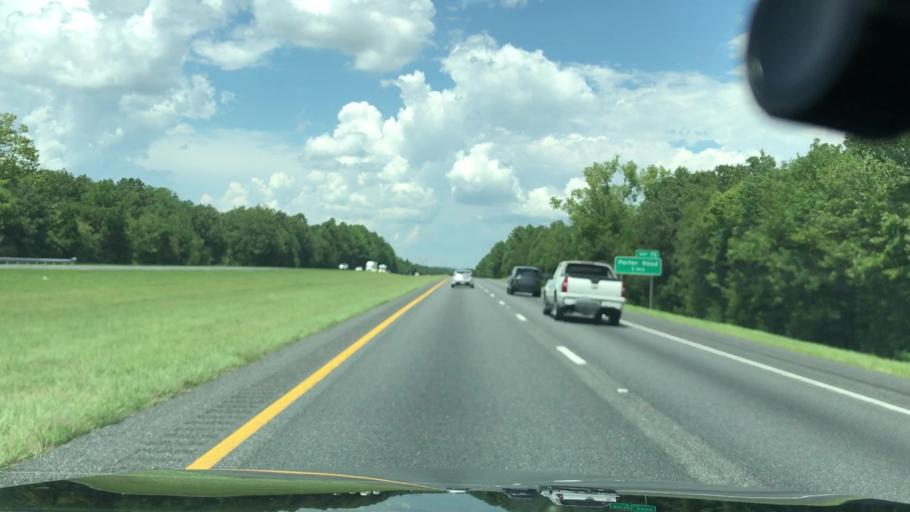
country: US
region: South Carolina
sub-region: York County
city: Lesslie
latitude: 34.8734
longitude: -81.0021
